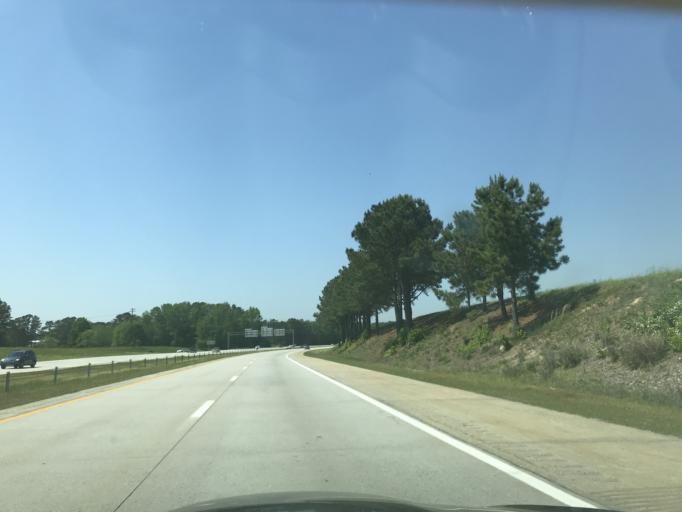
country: US
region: North Carolina
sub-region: Johnston County
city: Benson
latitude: 35.3921
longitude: -78.5197
